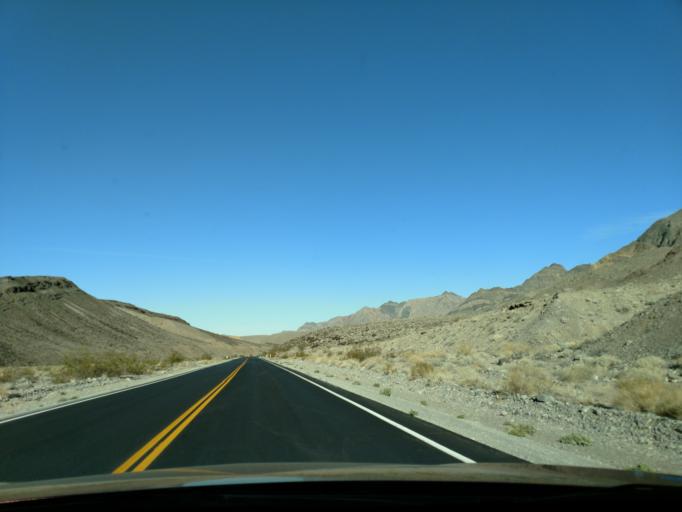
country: US
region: Nevada
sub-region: Nye County
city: Beatty
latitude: 36.3583
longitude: -116.6487
